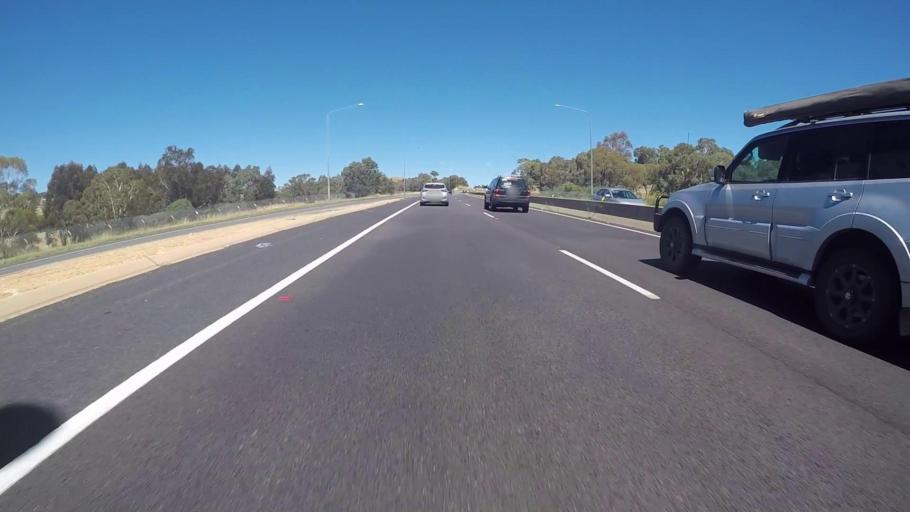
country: AU
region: Australian Capital Territory
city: Forrest
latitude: -35.3239
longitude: 149.0643
